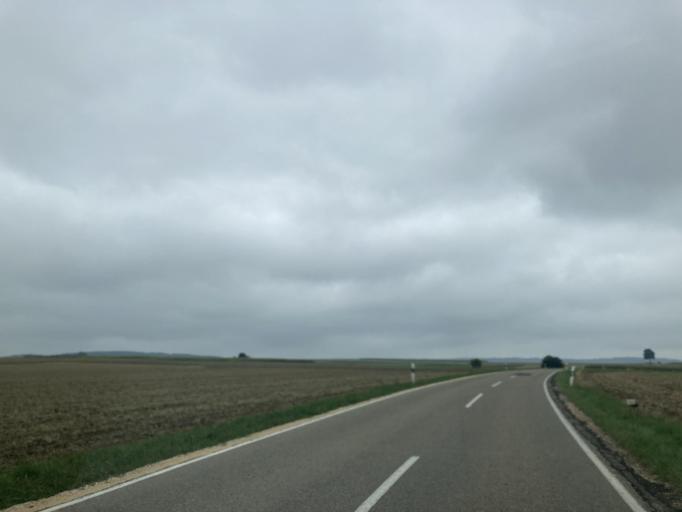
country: DE
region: Bavaria
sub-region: Swabia
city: Bachhagel
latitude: 48.6151
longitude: 10.3079
